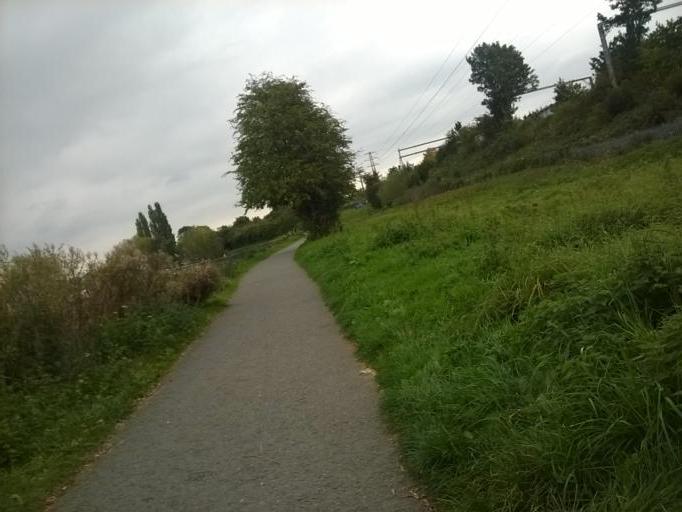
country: GB
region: England
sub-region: Reading
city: Reading
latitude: 51.4590
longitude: -0.9486
